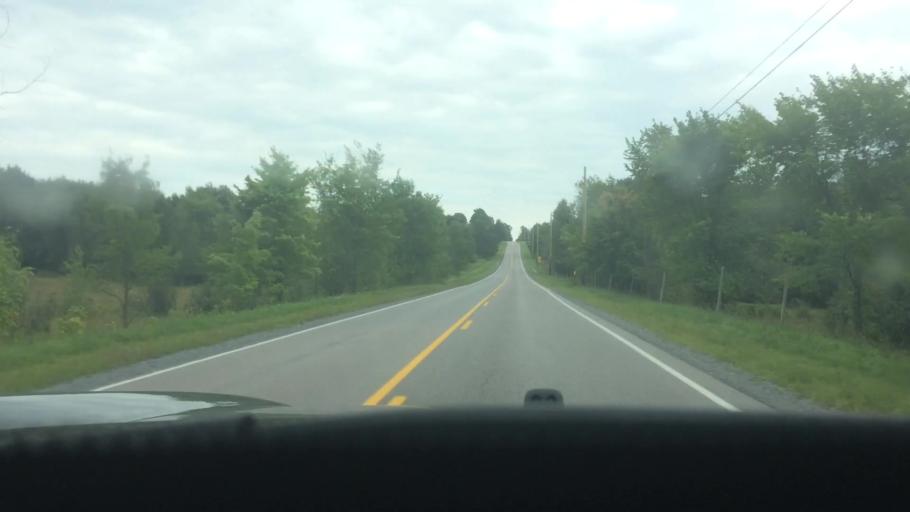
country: US
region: New York
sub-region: St. Lawrence County
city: Hannawa Falls
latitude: 44.5379
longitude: -75.0478
